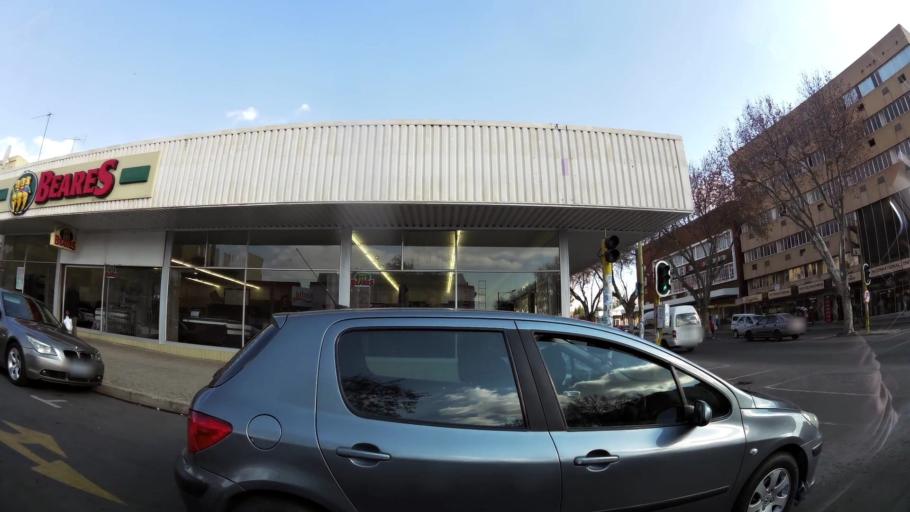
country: ZA
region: Gauteng
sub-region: West Rand District Municipality
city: Krugersdorp
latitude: -26.1030
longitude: 27.7707
